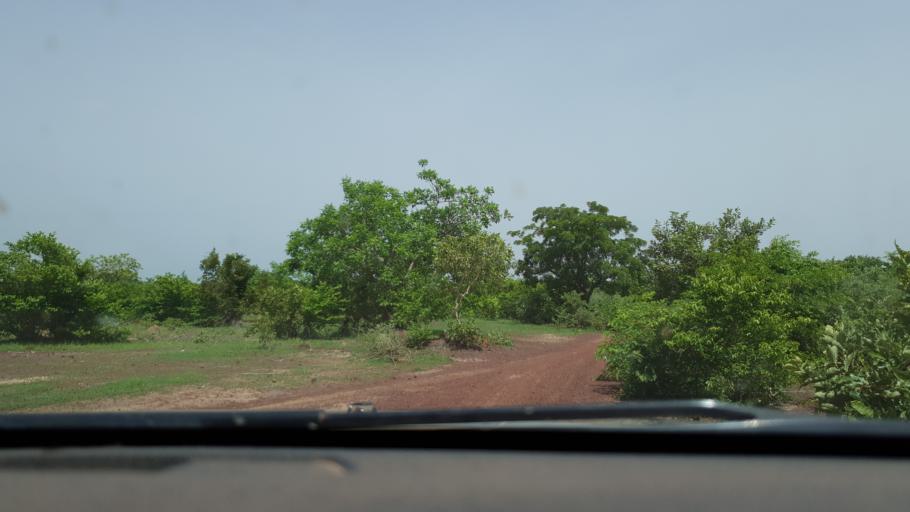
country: ML
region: Koulikoro
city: Koulikoro
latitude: 12.6666
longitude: -7.2367
